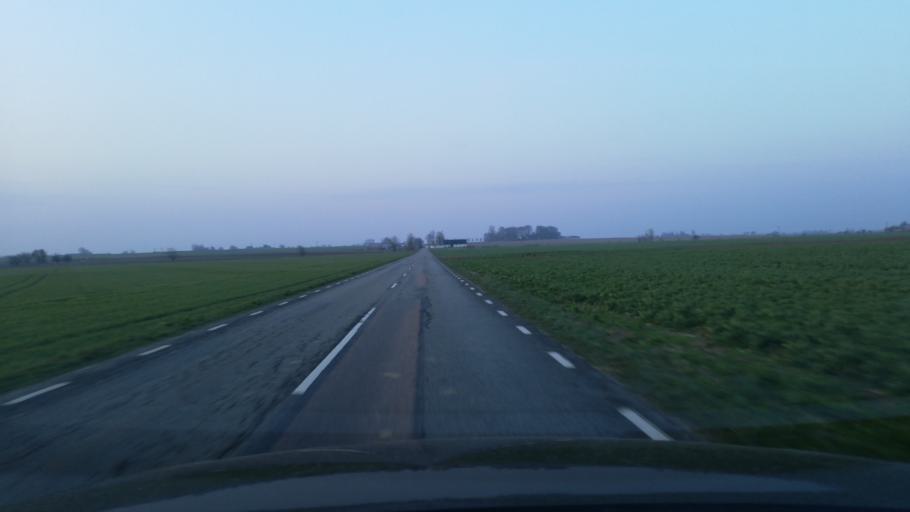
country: SE
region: Skane
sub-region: Tomelilla Kommun
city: Tomelilla
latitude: 55.4777
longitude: 14.0999
